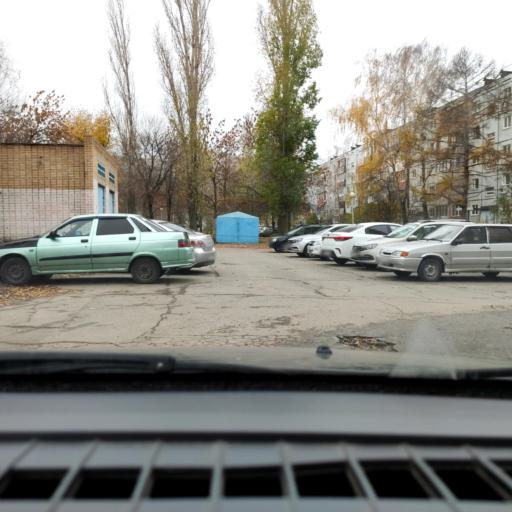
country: RU
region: Samara
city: Tol'yatti
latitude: 53.5288
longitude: 49.2670
